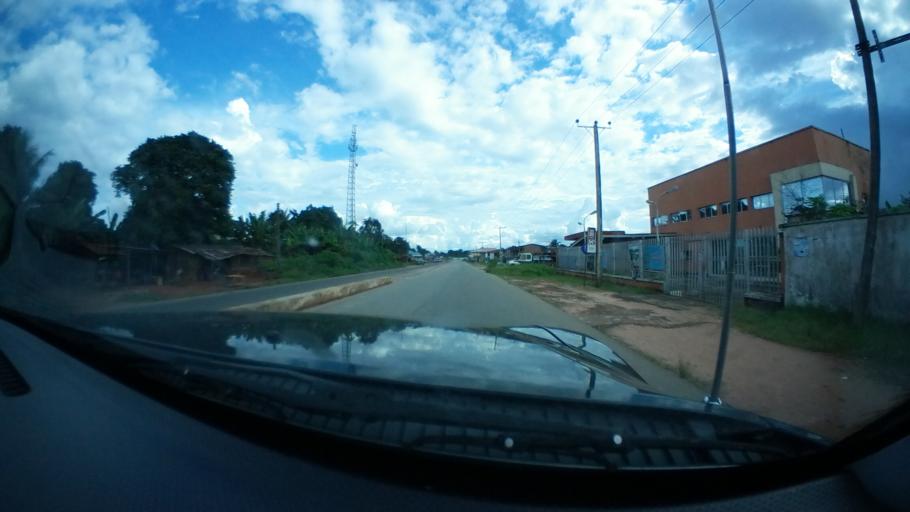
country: NG
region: Anambra
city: Uga
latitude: 5.8601
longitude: 7.1021
